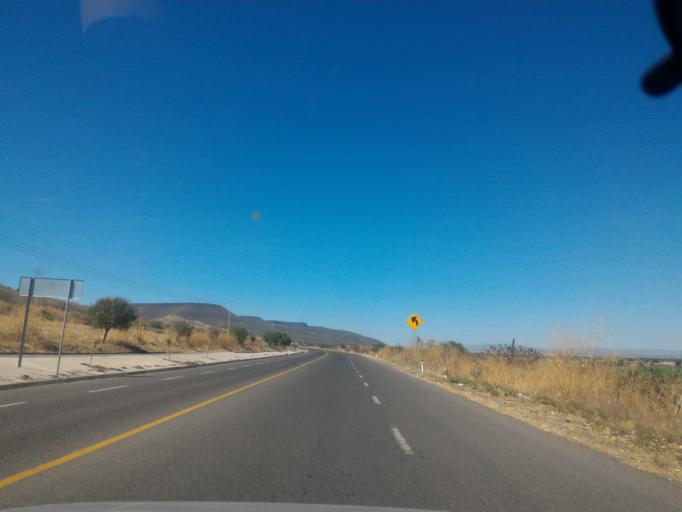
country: MX
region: Guanajuato
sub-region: San Francisco del Rincon
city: San Ignacio de Hidalgo
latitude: 20.9080
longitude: -101.9172
